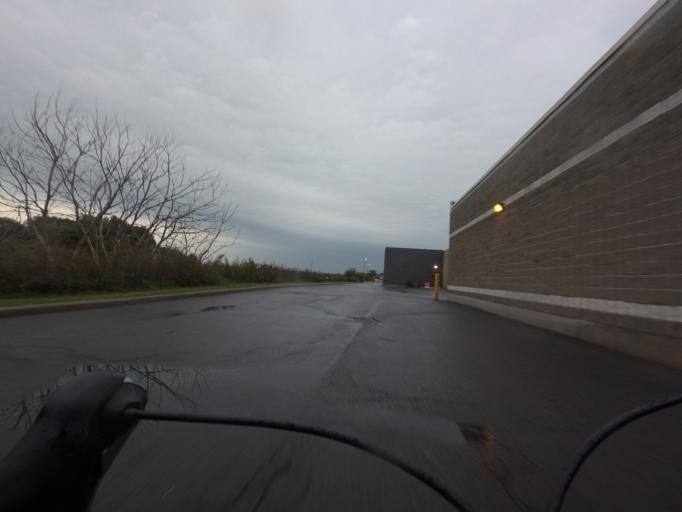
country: CA
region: Ontario
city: Bells Corners
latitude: 45.2676
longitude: -75.7484
